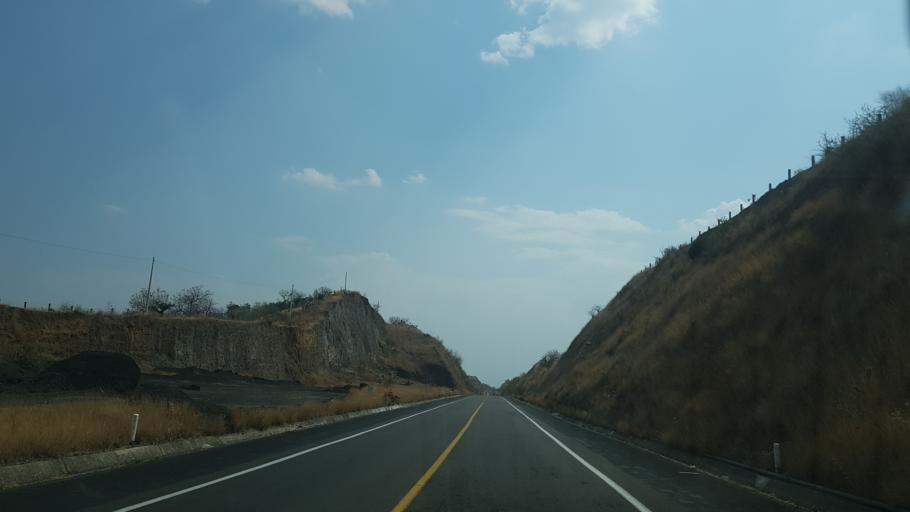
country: MX
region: Morelos
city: Tlacotepec
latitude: 18.8084
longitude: -98.7040
